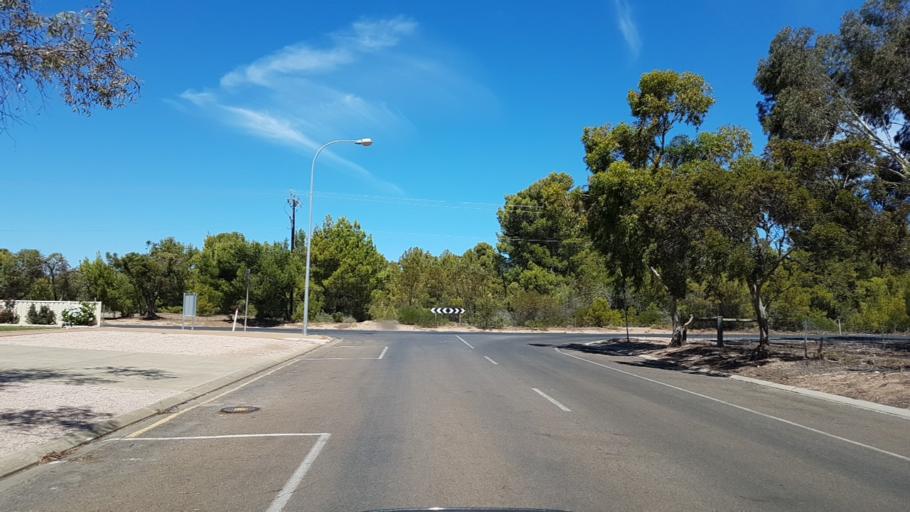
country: AU
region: South Australia
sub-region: Copper Coast
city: Wallaroo
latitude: -34.0628
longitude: 137.5907
